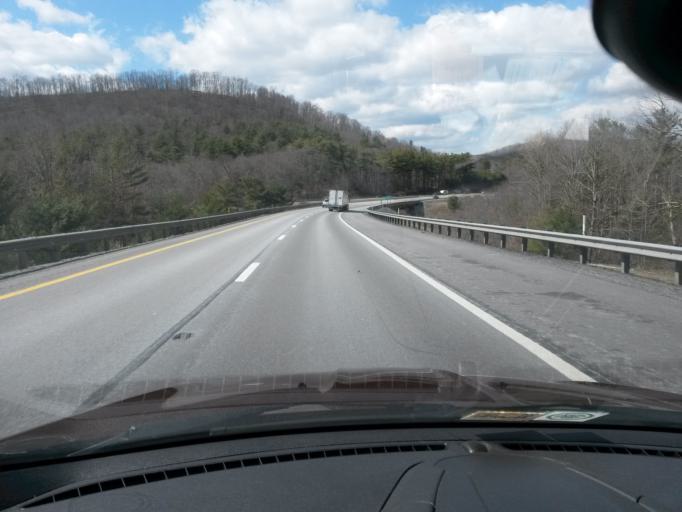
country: US
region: West Virginia
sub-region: Raleigh County
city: Beaver
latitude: 37.7092
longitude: -81.1499
